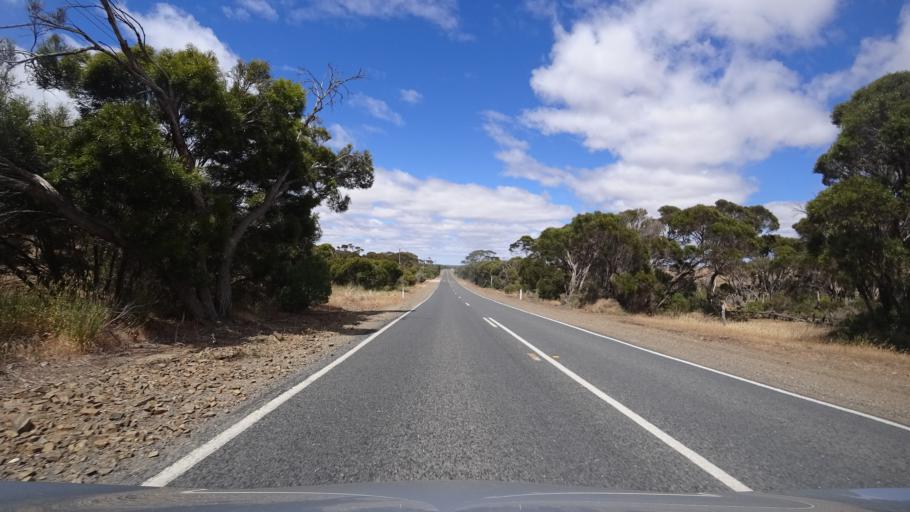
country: AU
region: South Australia
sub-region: Kangaroo Island
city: Kingscote
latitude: -35.6642
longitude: 137.5984
